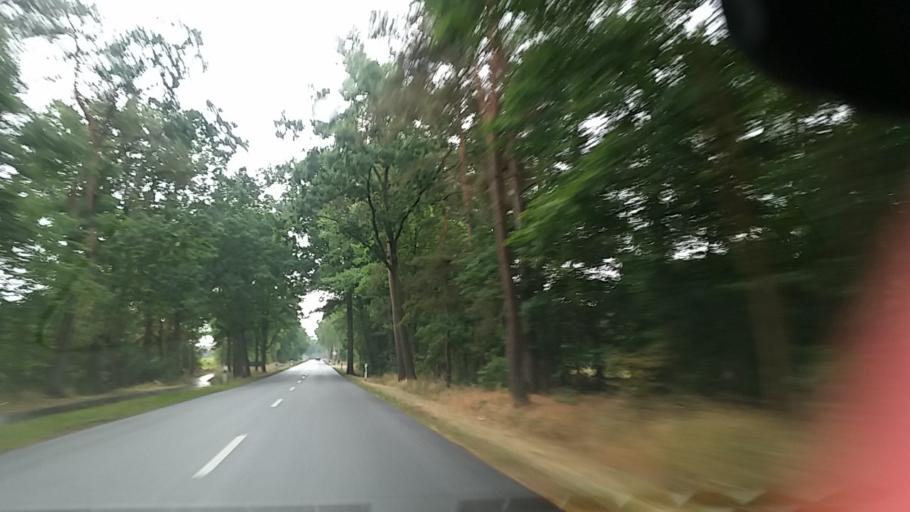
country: DE
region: Lower Saxony
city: Bokensdorf
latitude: 52.5084
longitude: 10.7161
